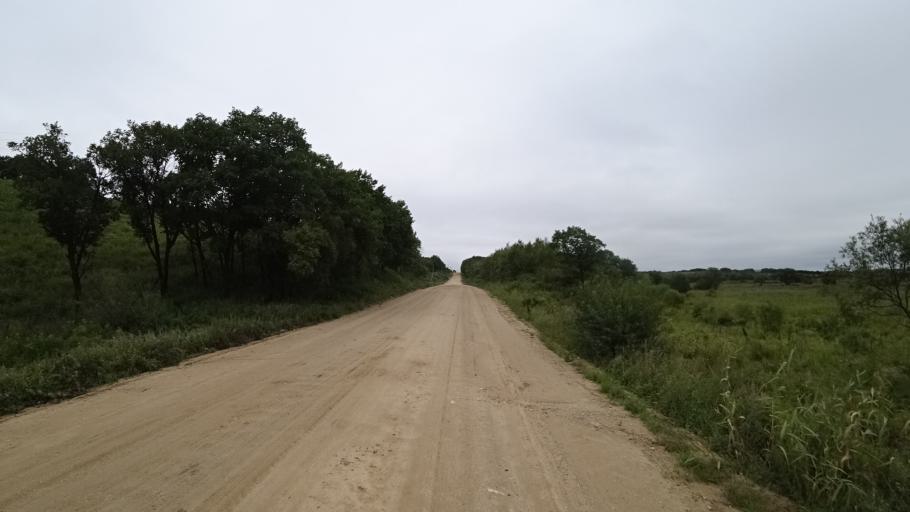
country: RU
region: Primorskiy
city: Ivanovka
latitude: 44.0717
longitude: 132.5813
